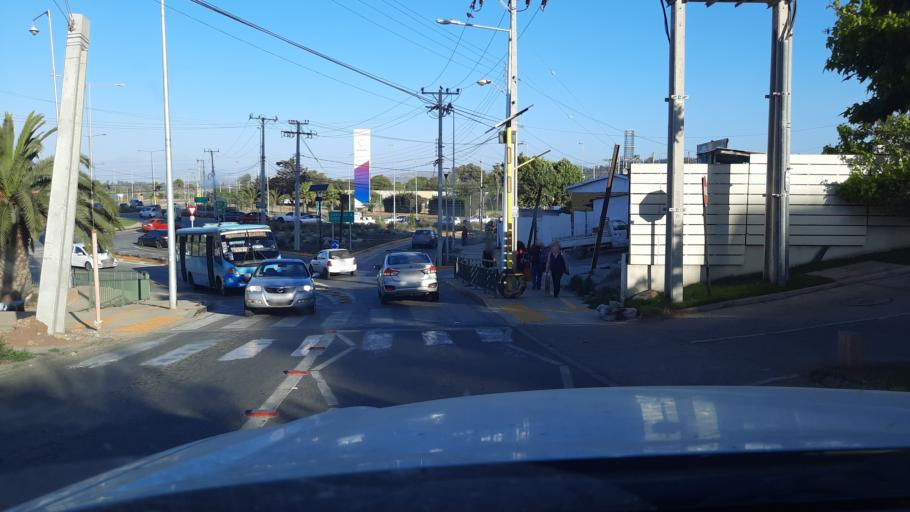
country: CL
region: Valparaiso
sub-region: Provincia de Valparaiso
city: Vina del Mar
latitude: -32.9217
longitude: -71.5078
